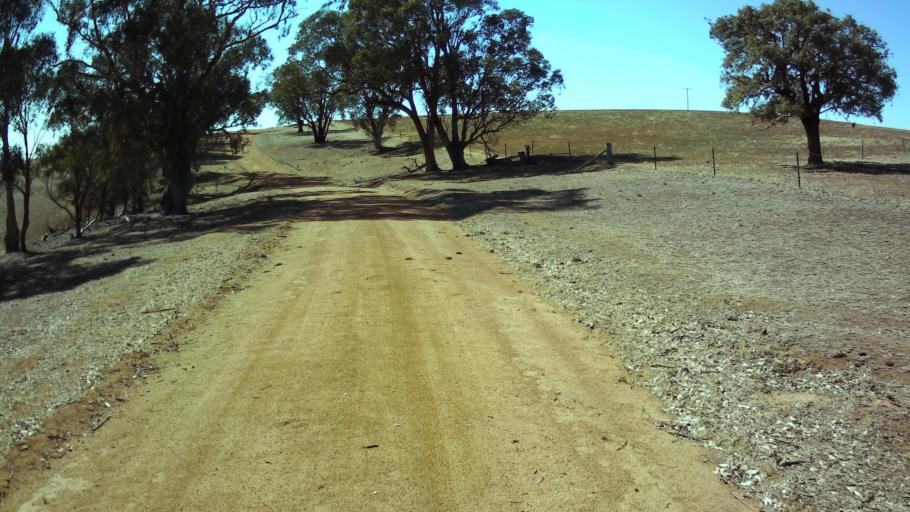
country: AU
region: New South Wales
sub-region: Cowra
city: Cowra
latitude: -33.9748
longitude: 148.4630
